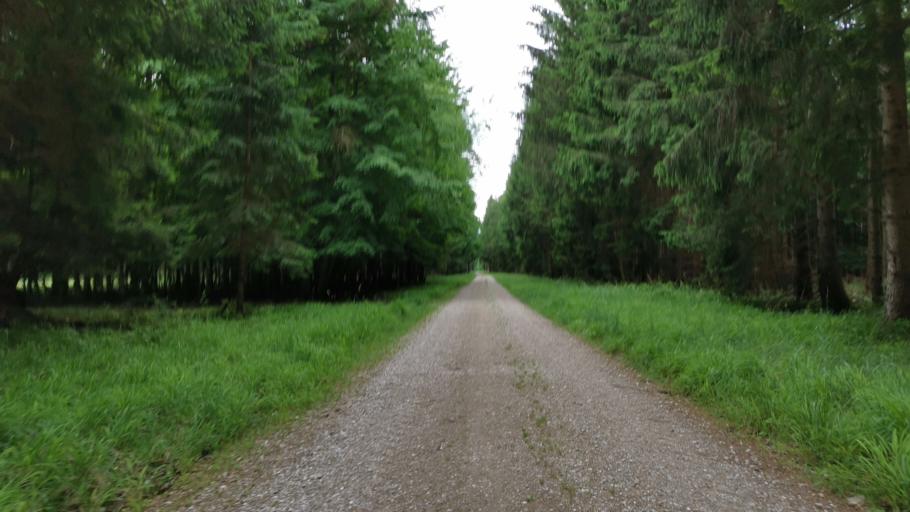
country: DE
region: Bavaria
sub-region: Upper Bavaria
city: Baierbrunn
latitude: 48.0503
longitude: 11.4928
